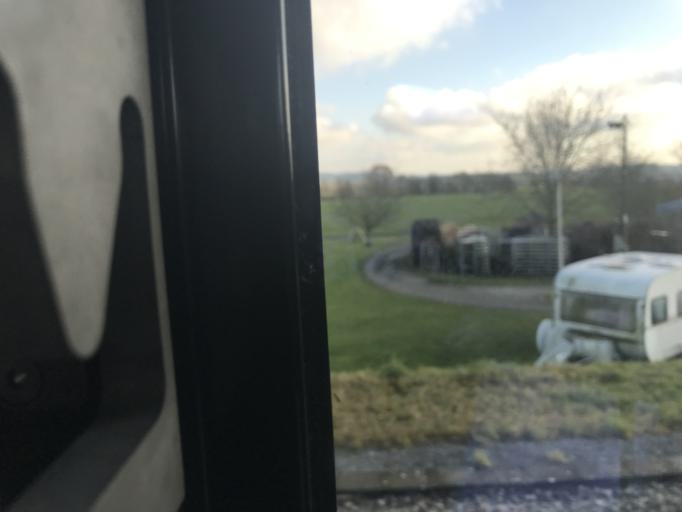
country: CH
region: Zurich
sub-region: Bezirk Andelfingen
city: Dachsen
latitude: 47.6650
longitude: 8.5974
